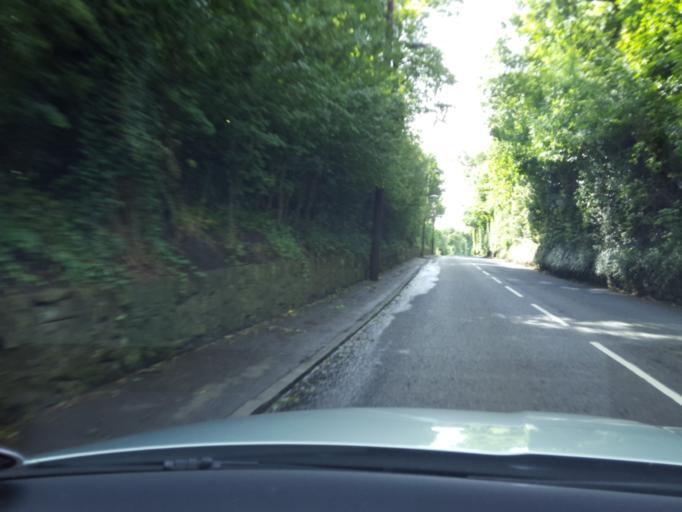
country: GB
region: Scotland
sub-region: Falkirk
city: Bo'ness
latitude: 56.0119
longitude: -3.5759
